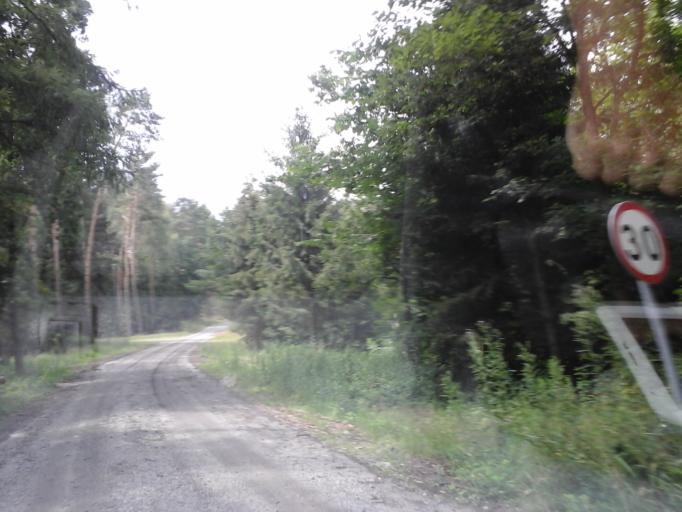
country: PL
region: West Pomeranian Voivodeship
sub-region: Powiat choszczenski
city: Bierzwnik
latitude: 52.9499
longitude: 15.6458
